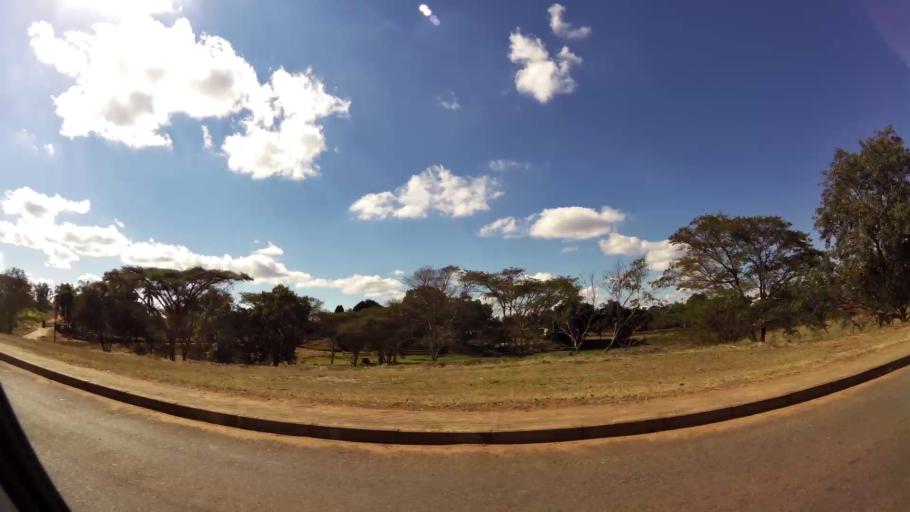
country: ZA
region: Limpopo
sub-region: Mopani District Municipality
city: Tzaneen
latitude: -23.8184
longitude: 30.1614
